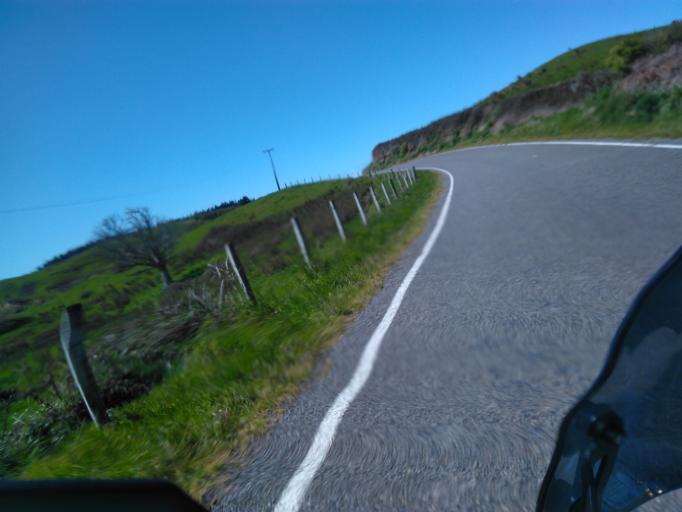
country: NZ
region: Gisborne
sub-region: Gisborne District
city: Gisborne
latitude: -38.5311
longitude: 178.2145
